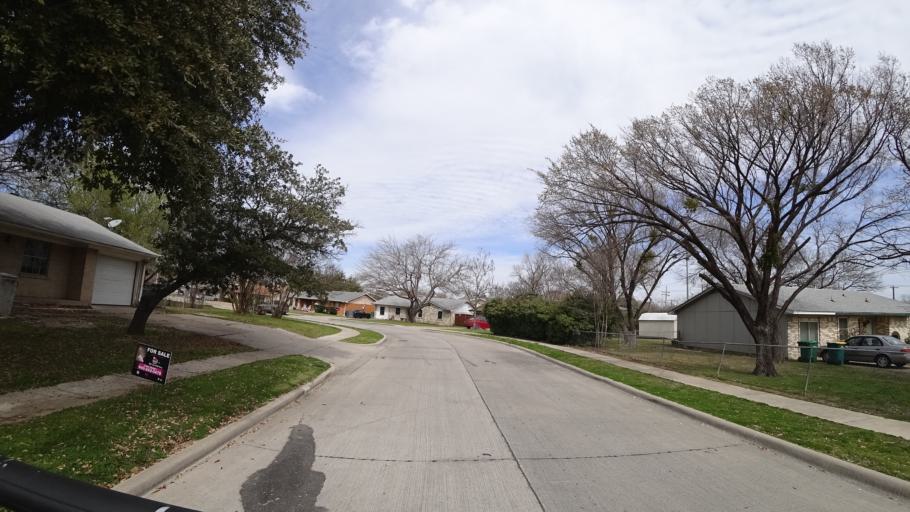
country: US
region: Texas
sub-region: Denton County
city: Lewisville
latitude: 33.0380
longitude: -97.0110
